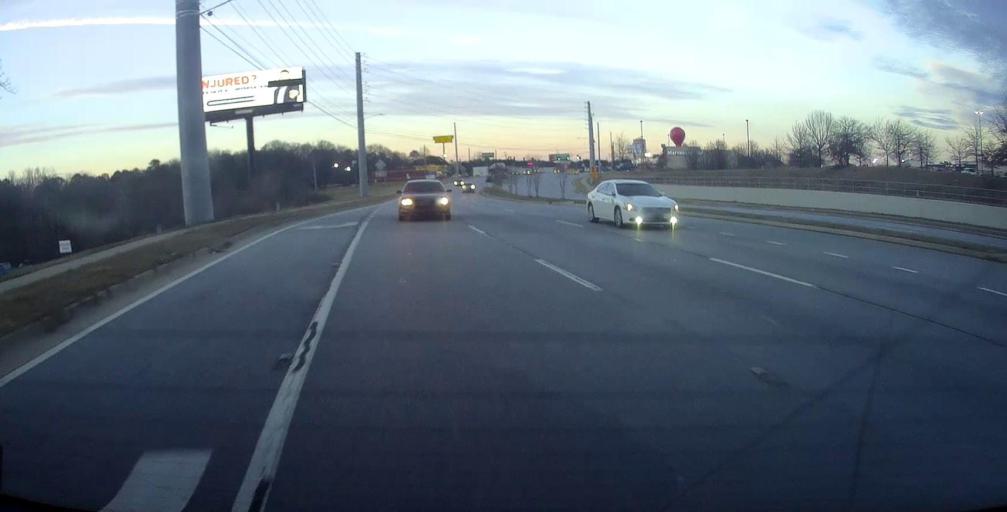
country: US
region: Alabama
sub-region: Russell County
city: Phenix City
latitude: 32.5405
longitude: -84.9548
